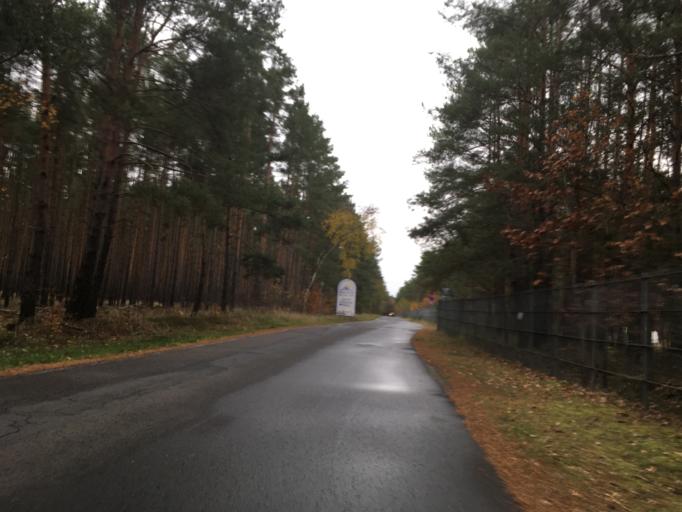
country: DE
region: Brandenburg
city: Mullrose
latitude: 52.2705
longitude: 14.4788
